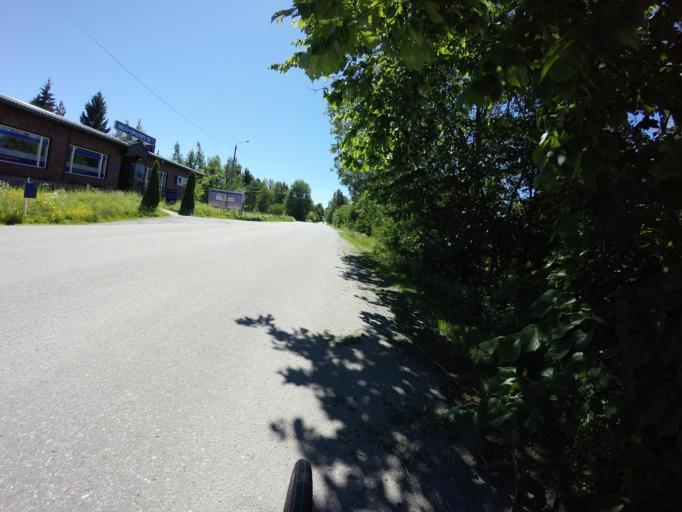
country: FI
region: Varsinais-Suomi
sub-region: Turku
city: Turku
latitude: 60.4769
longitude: 22.2951
